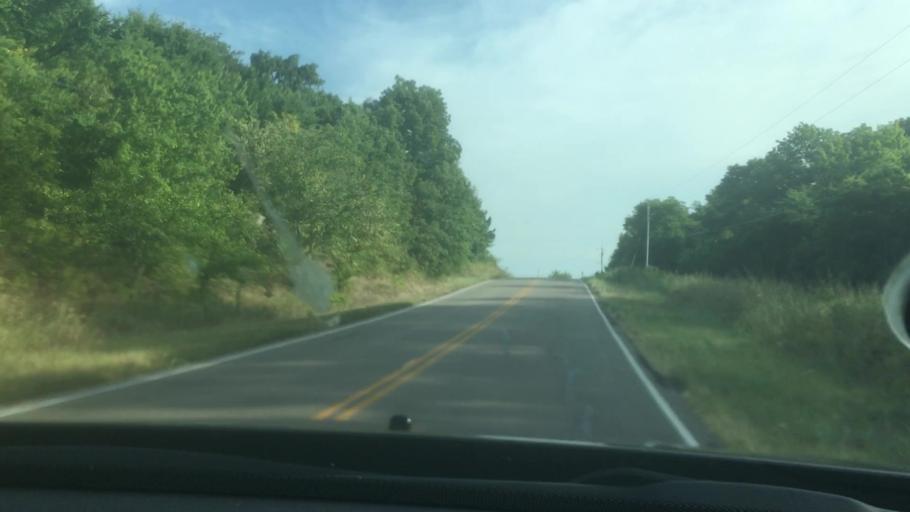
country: US
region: Oklahoma
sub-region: Pontotoc County
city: Ada
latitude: 34.7311
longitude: -96.6700
